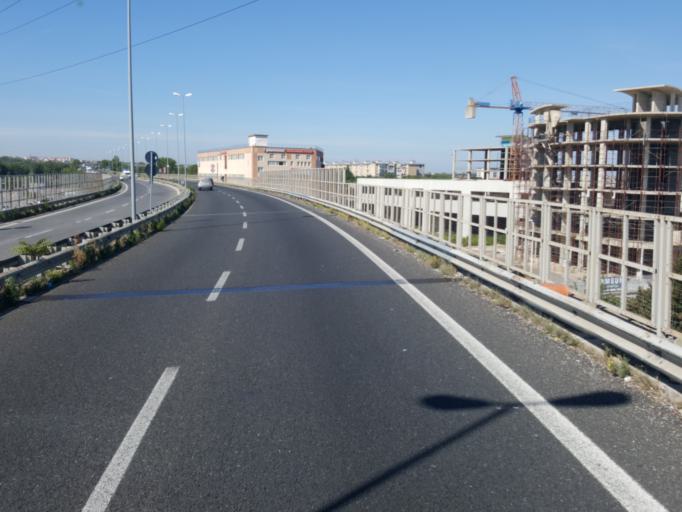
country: IT
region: Campania
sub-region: Provincia di Napoli
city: Frattamaggiore
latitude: 40.9283
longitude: 14.2741
